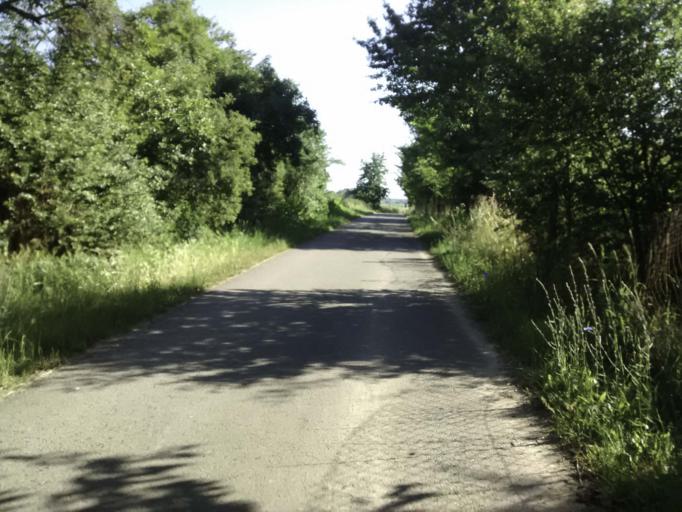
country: DE
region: Saxony-Anhalt
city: Rogatz
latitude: 52.3221
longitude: 11.7770
